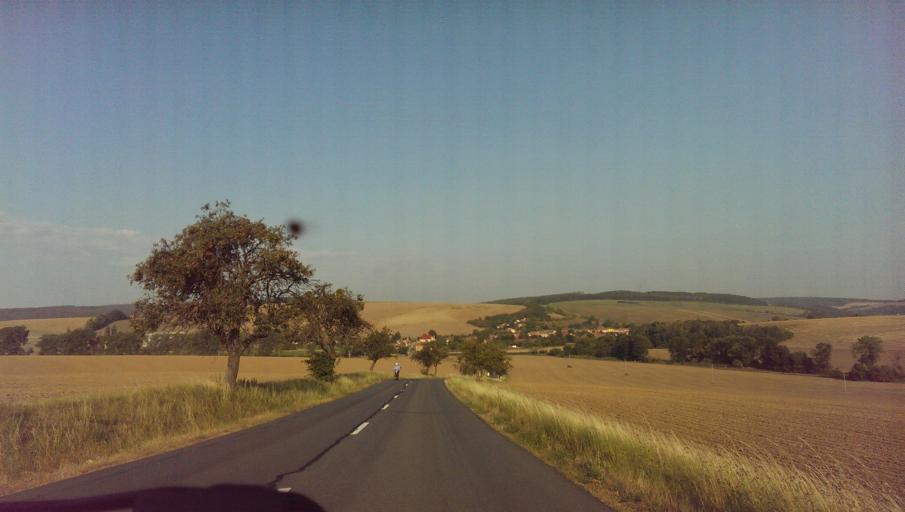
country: CZ
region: Zlin
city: Korycany
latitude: 49.1089
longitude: 17.1489
